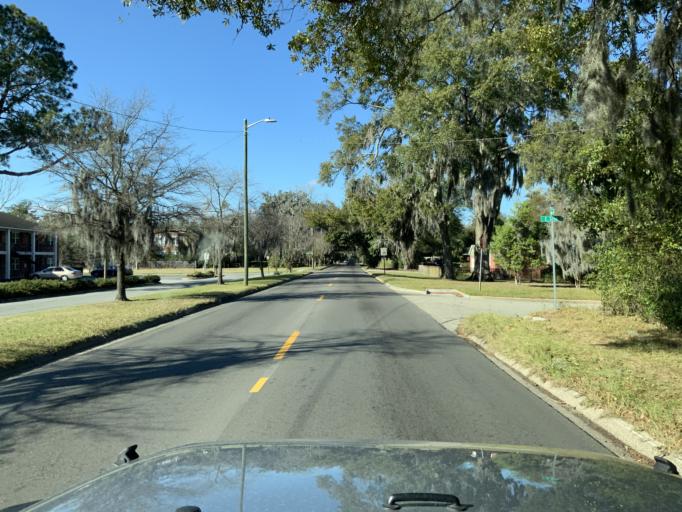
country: US
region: Georgia
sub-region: Chatham County
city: Thunderbolt
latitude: 32.0522
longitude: -81.0665
